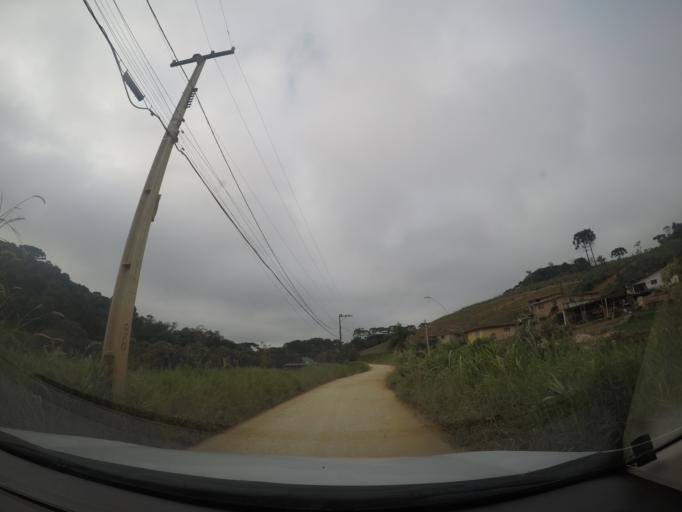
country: BR
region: Parana
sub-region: Colombo
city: Colombo
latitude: -25.3202
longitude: -49.2539
